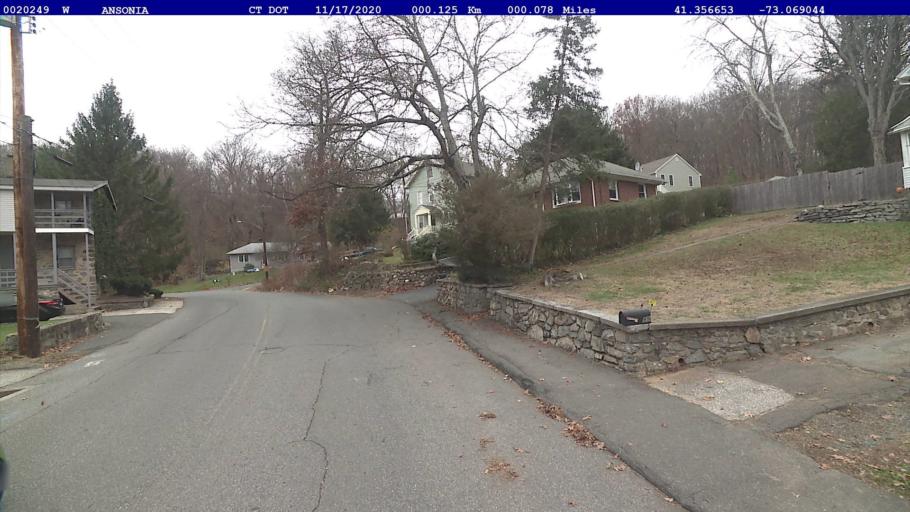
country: US
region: Connecticut
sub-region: New Haven County
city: Ansonia
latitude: 41.3567
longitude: -73.0690
